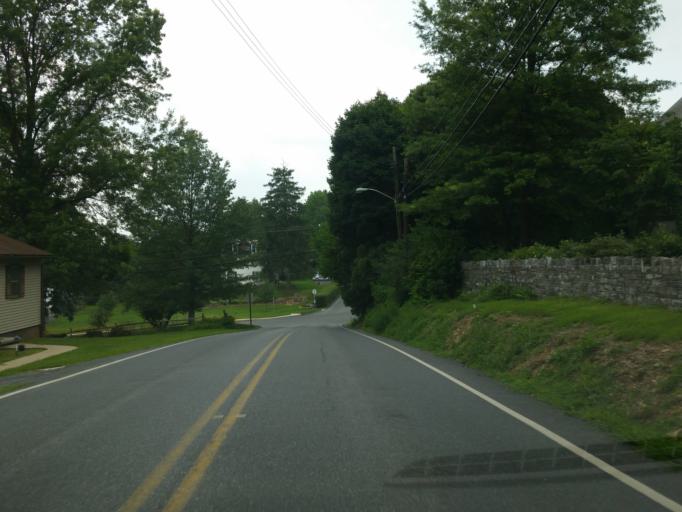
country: US
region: Pennsylvania
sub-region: Lebanon County
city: Palmyra
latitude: 40.3191
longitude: -76.6028
